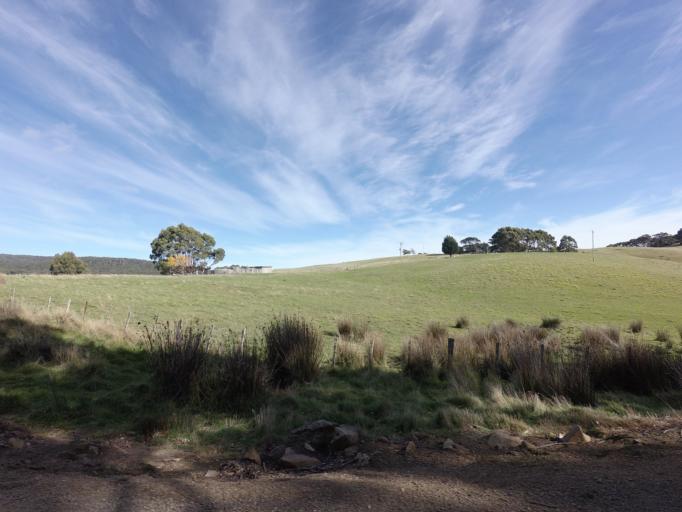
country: AU
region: Tasmania
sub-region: Clarence
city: Sandford
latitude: -43.1865
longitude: 147.7727
